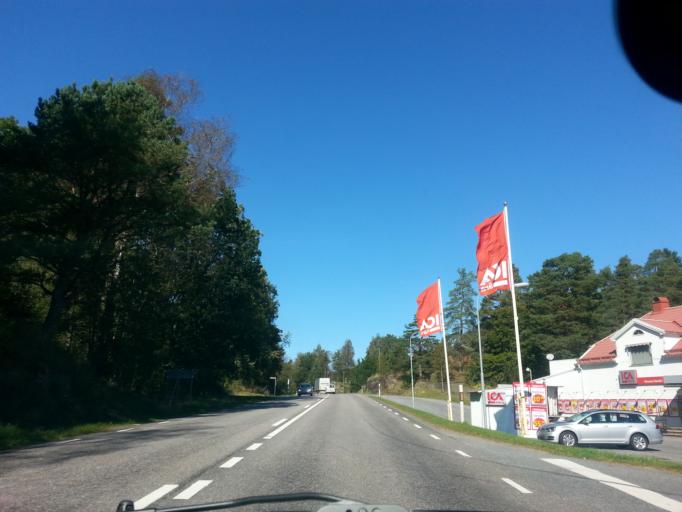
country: SE
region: Vaestra Goetaland
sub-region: Harryda Kommun
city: Ravlanda
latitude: 57.5490
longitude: 12.5318
